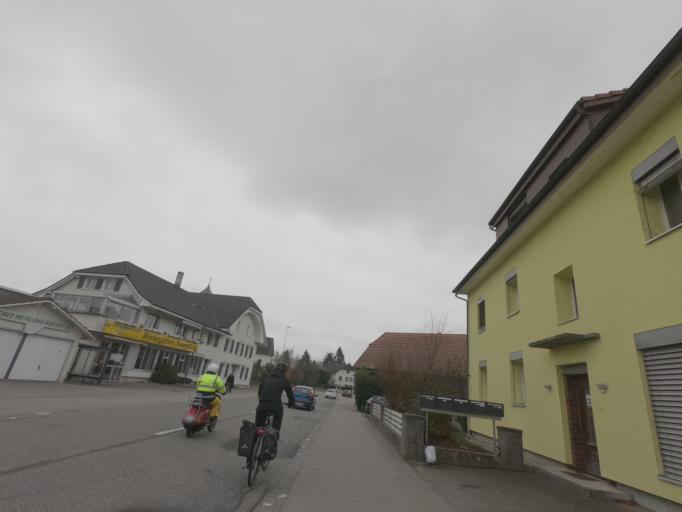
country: CH
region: Solothurn
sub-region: Bezirk Wasseramt
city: Biberist
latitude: 47.1845
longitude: 7.5572
